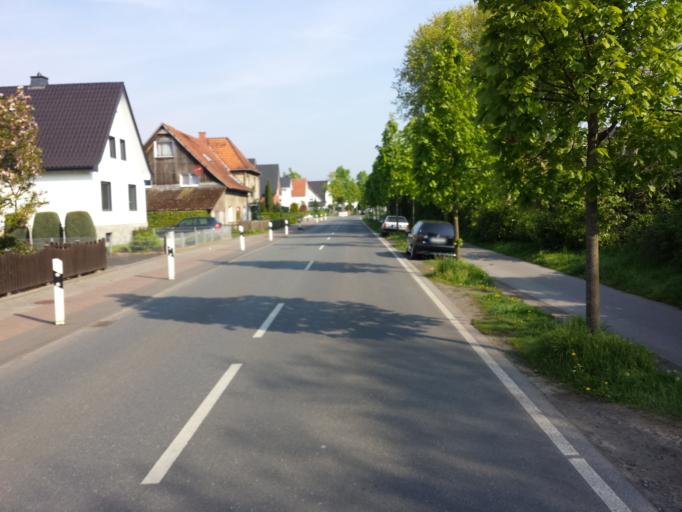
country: DE
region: North Rhine-Westphalia
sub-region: Regierungsbezirk Detmold
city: Guetersloh
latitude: 51.8813
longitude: 8.3771
